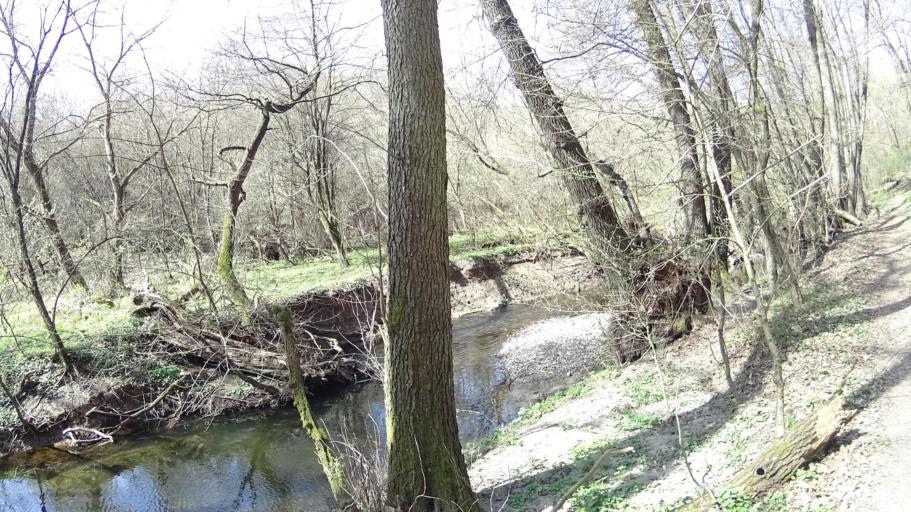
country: HU
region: Pest
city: Veroce
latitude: 47.8635
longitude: 19.0347
